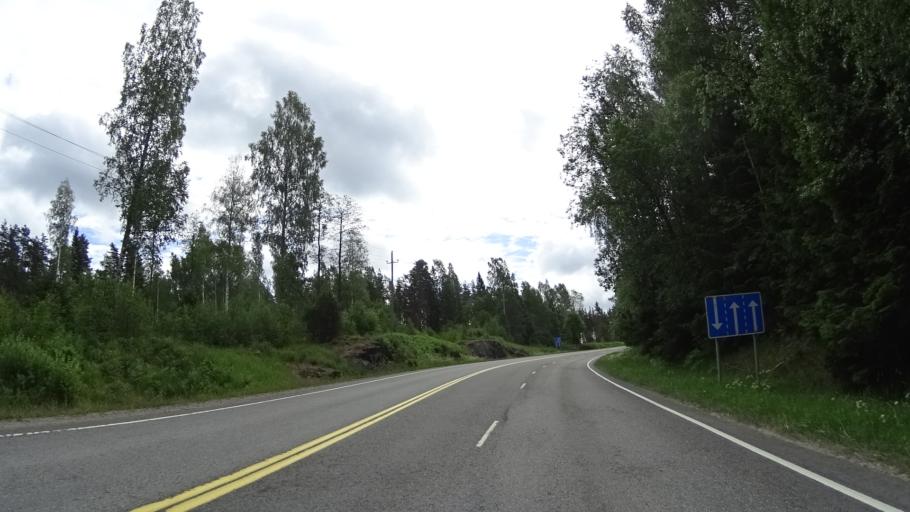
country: FI
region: Uusimaa
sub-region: Helsinki
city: Vihti
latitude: 60.2924
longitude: 24.4029
